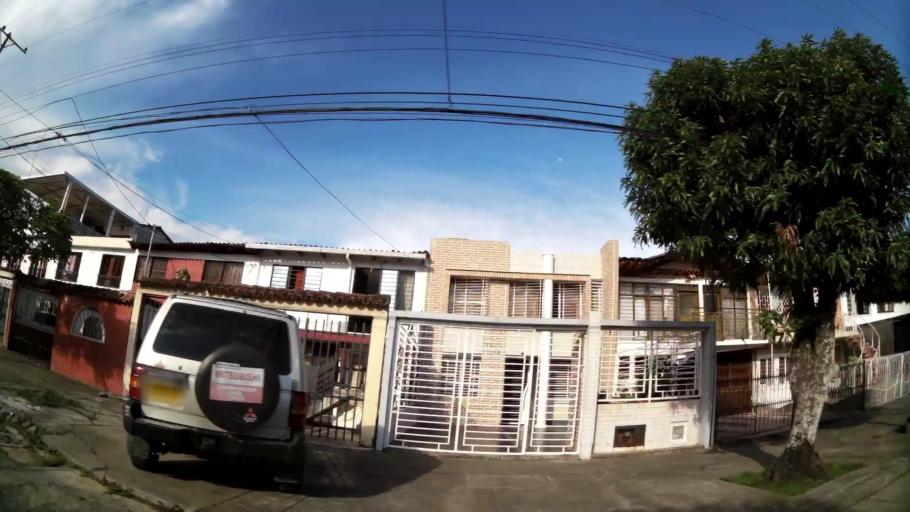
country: CO
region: Valle del Cauca
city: Cali
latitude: 3.4325
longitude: -76.5239
